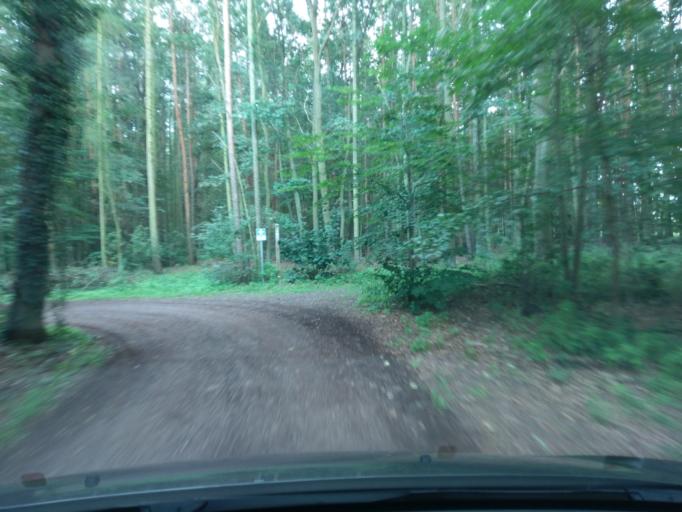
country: DE
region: Brandenburg
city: Gross Kreutz
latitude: 52.3205
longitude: 12.7663
